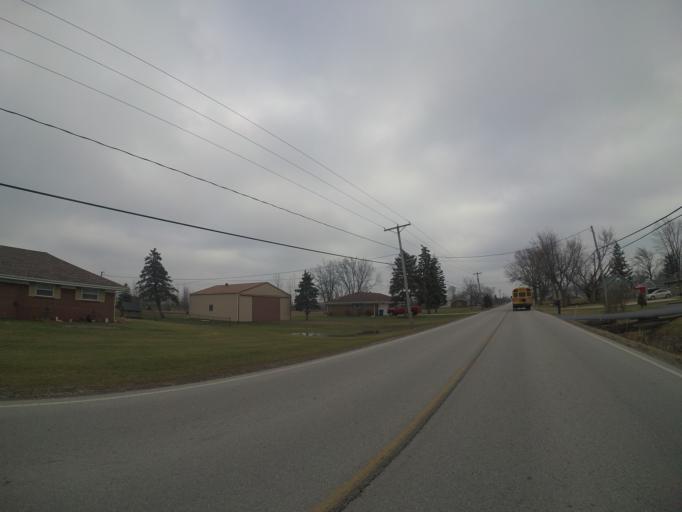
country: US
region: Ohio
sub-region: Wood County
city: Walbridge
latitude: 41.5724
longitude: -83.5121
